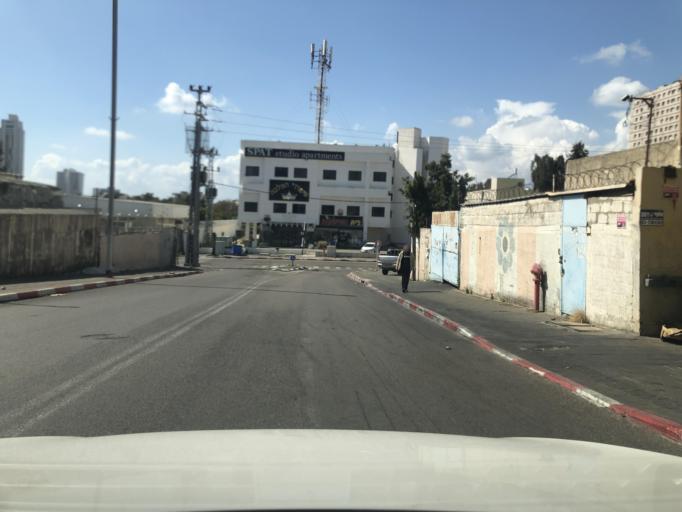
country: IL
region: Tel Aviv
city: Bat Yam
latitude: 32.0115
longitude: 34.7511
